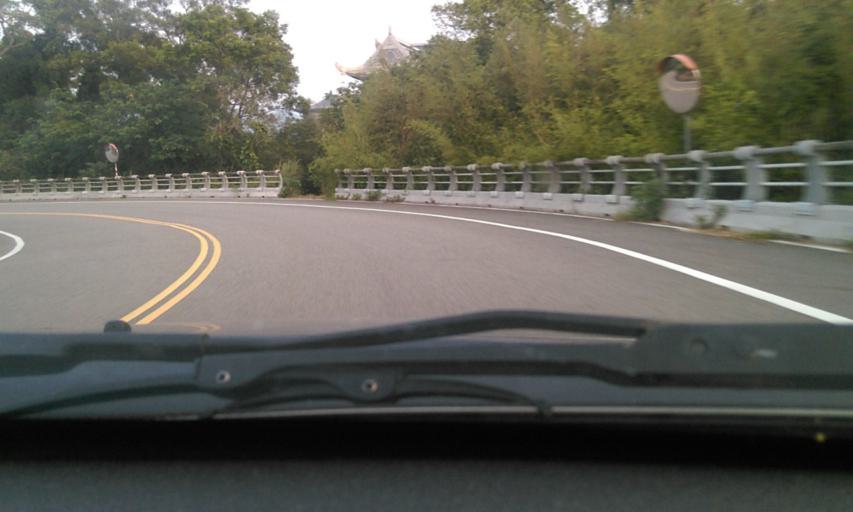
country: TW
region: Taiwan
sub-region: Hsinchu
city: Hsinchu
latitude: 24.6846
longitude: 120.9849
